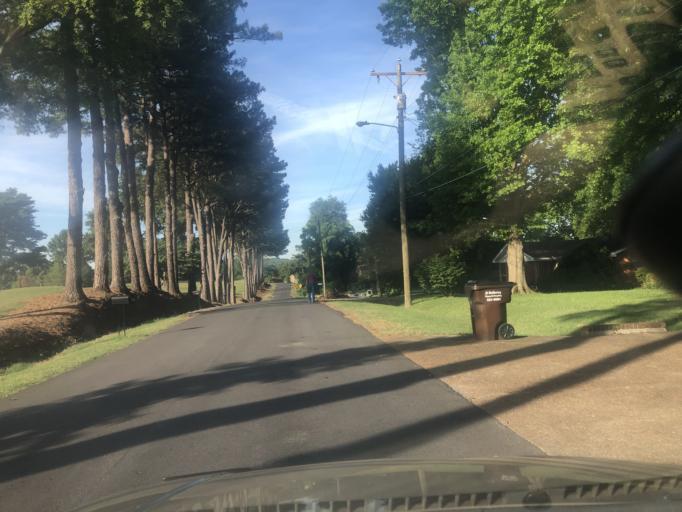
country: US
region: Tennessee
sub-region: Davidson County
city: Lakewood
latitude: 36.2535
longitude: -86.6507
